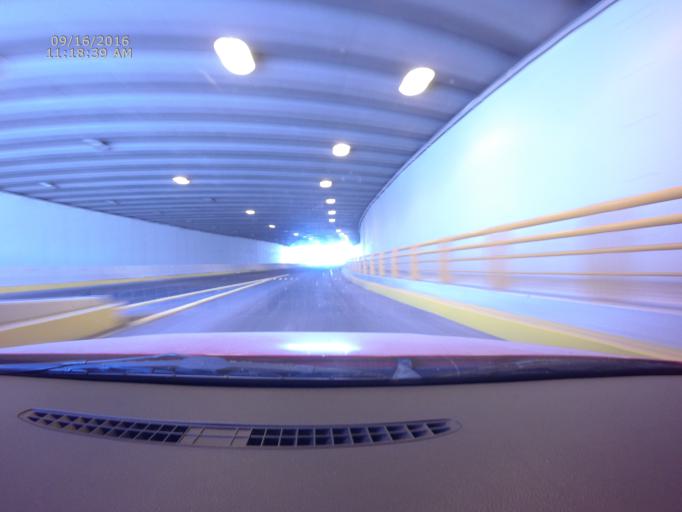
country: MX
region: Queretaro
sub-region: Queretaro
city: El Salitre
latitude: 20.6770
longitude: -100.4336
